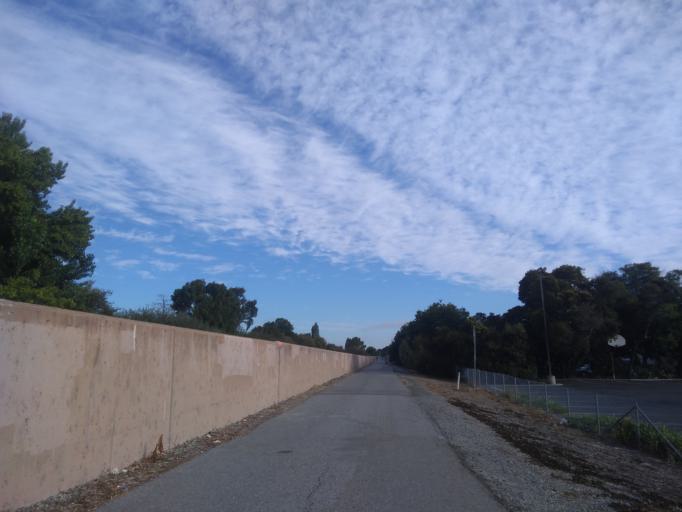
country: US
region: California
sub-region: Santa Clara County
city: Santa Clara
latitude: 37.3960
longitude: -121.9865
